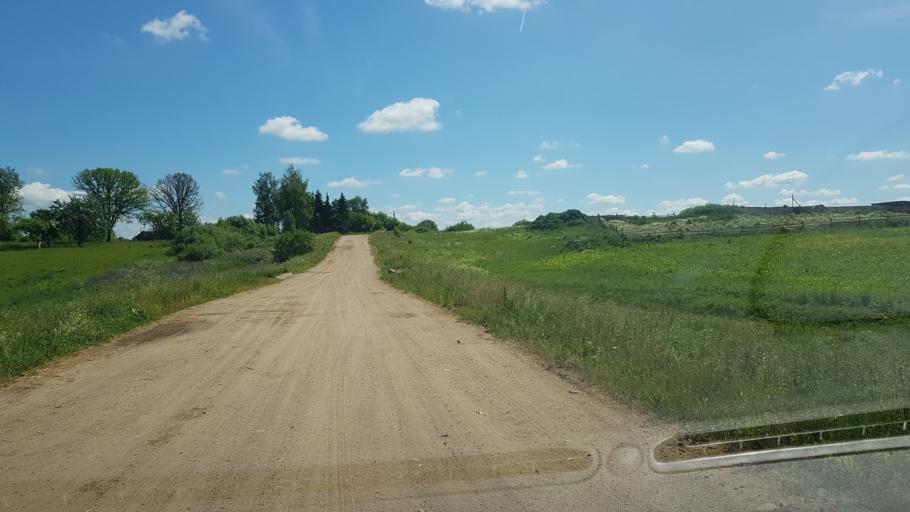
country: BY
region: Vitebsk
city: Dubrowna
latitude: 54.4832
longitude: 30.7968
